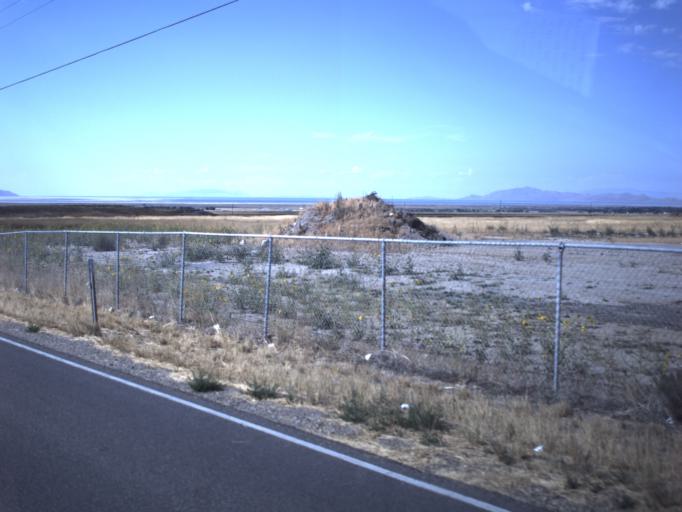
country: US
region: Utah
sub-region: Tooele County
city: Tooele
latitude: 40.5543
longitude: -112.3474
